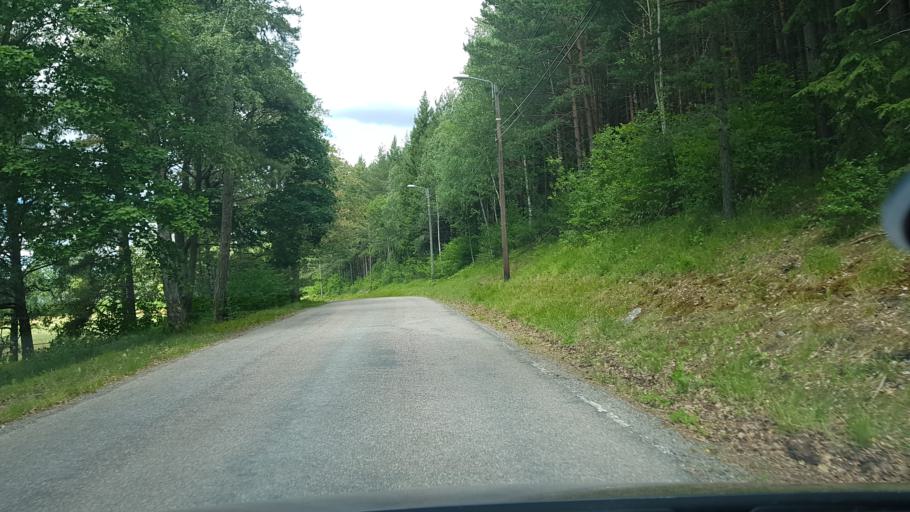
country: SE
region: Stockholm
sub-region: Upplands-Bro Kommun
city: Kungsaengen
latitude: 59.4890
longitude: 17.8041
